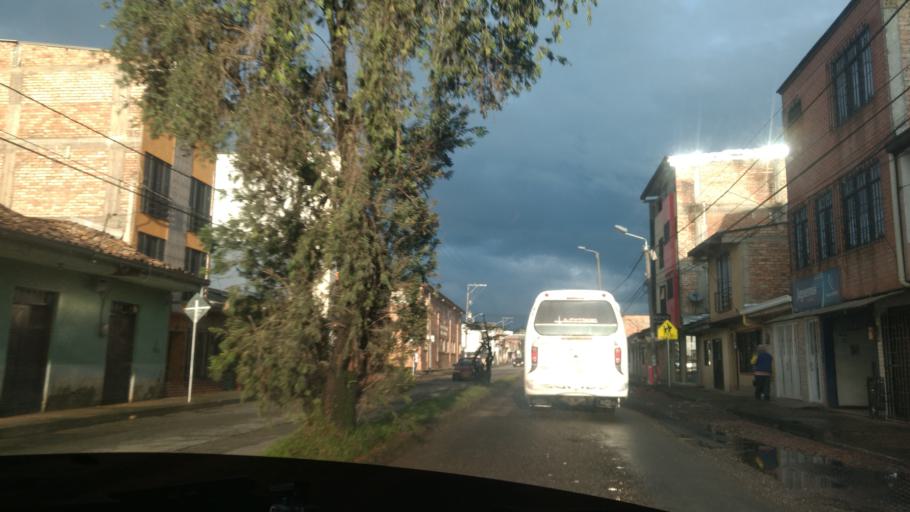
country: CO
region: Cauca
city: Popayan
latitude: 2.4524
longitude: -76.5970
